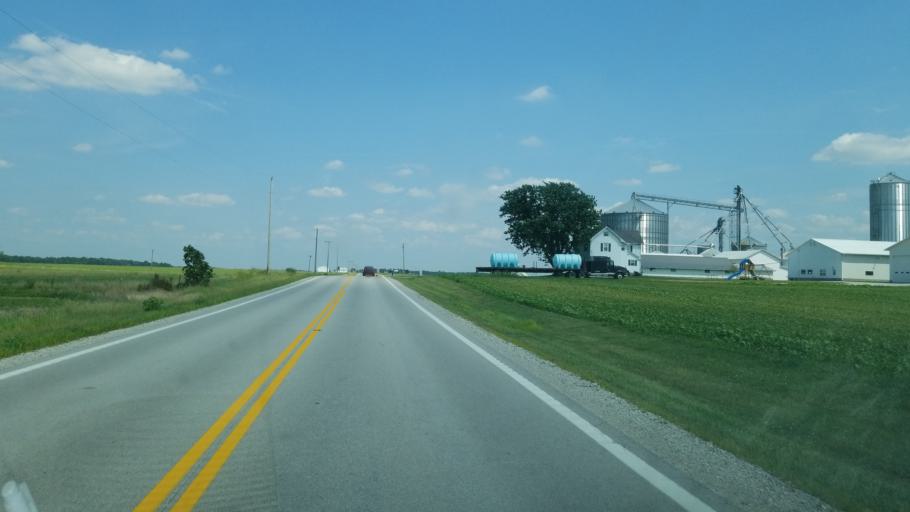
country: US
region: Ohio
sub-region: Sandusky County
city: Mount Carmel
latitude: 41.1246
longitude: -82.9102
